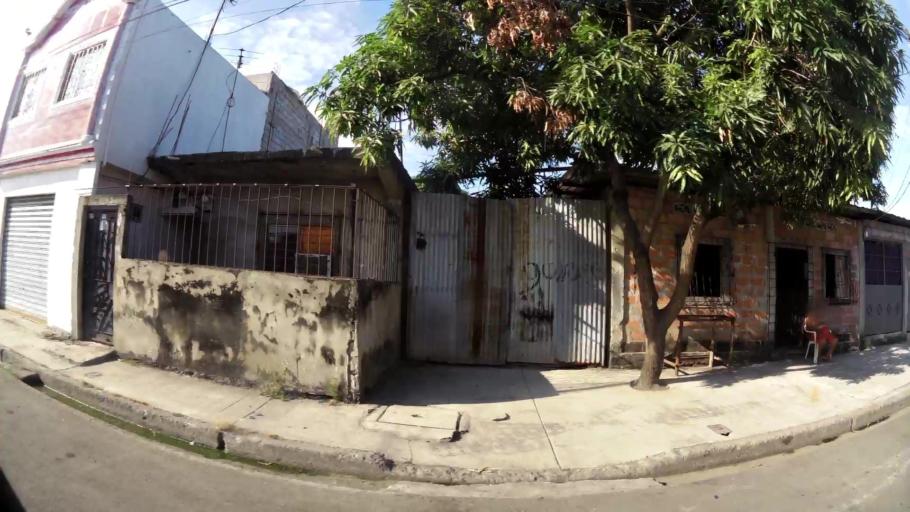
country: EC
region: Guayas
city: Guayaquil
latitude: -2.2170
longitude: -79.9214
